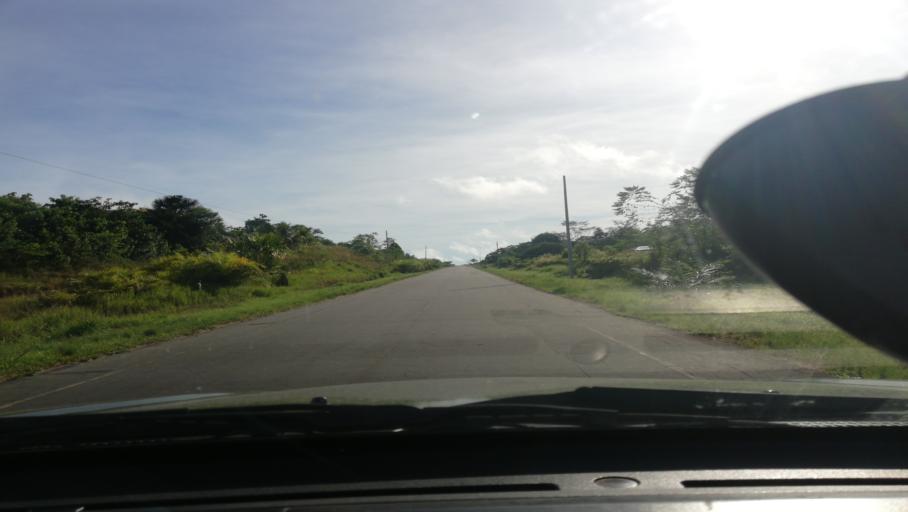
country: PE
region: Loreto
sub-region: Provincia de Loreto
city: Nauta
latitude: -4.3510
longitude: -73.5456
